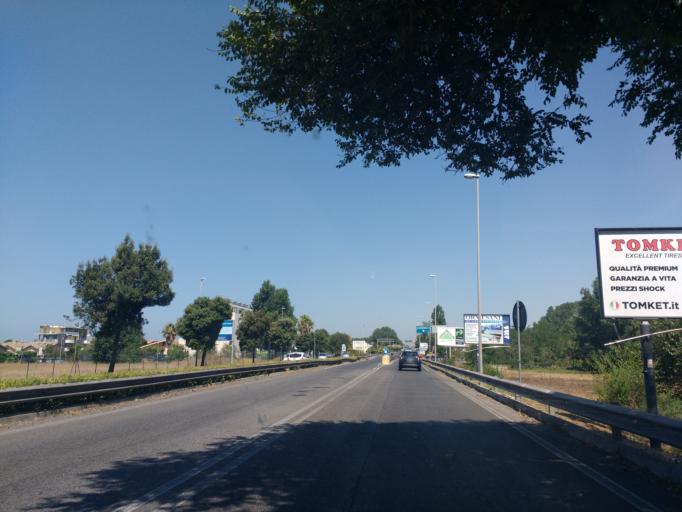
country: IT
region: Latium
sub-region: Citta metropolitana di Roma Capitale
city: Fiumicino-Isola Sacra
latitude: 41.7681
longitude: 12.2609
